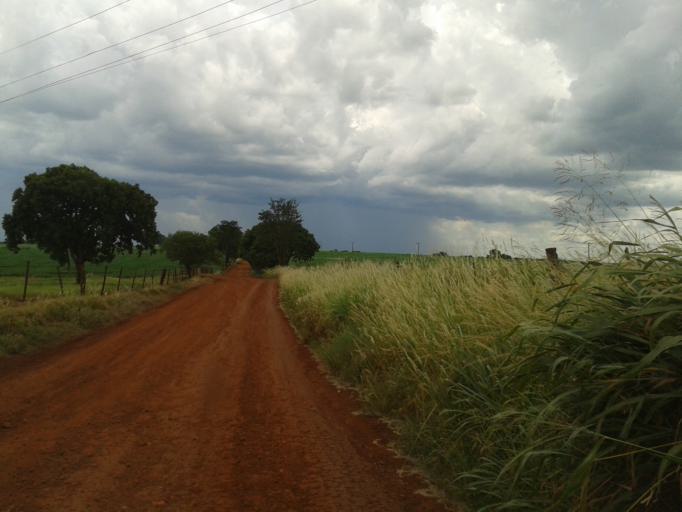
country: BR
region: Minas Gerais
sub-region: Centralina
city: Centralina
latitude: -18.7067
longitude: -49.2158
